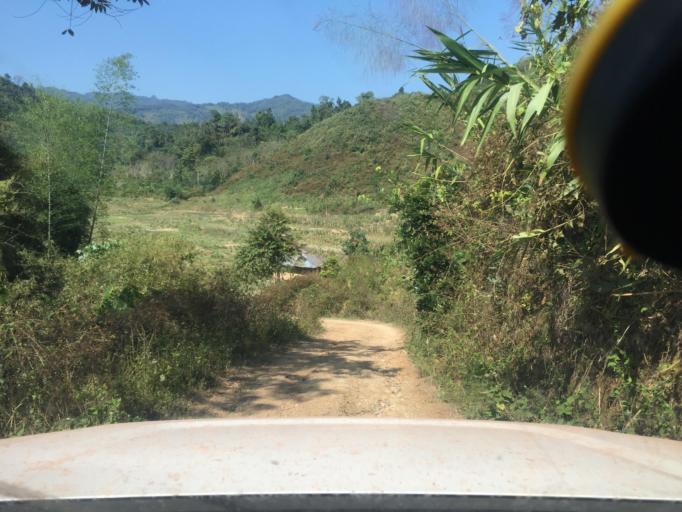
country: LA
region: Phongsali
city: Phongsali
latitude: 21.6498
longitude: 102.4081
